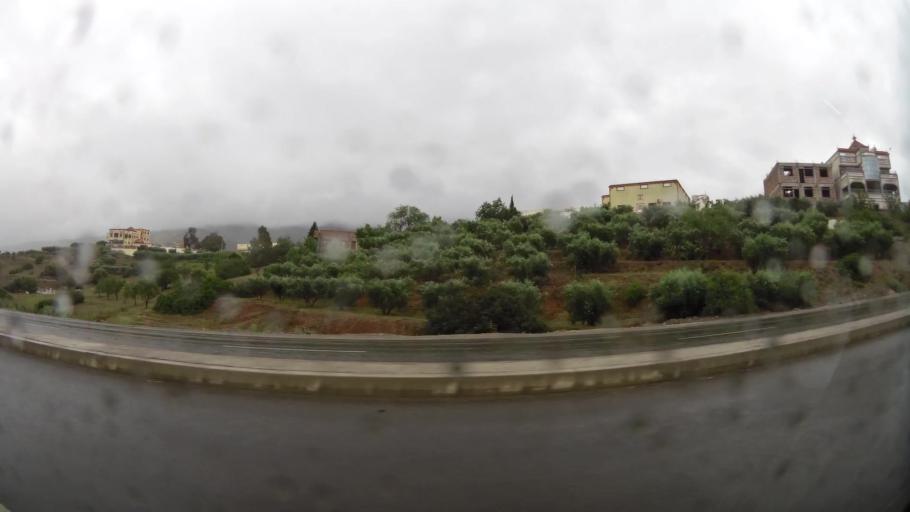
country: MA
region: Taza-Al Hoceima-Taounate
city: Imzourene
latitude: 35.0392
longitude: -3.8214
